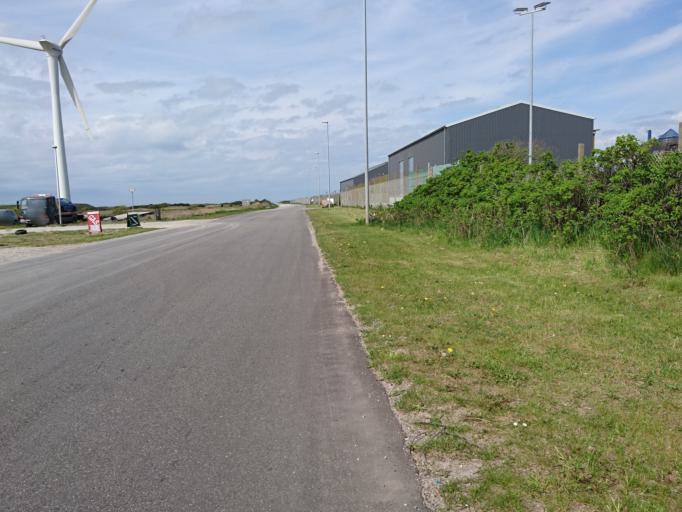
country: DK
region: North Denmark
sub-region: Frederikshavn Kommune
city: Skagen
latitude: 57.7360
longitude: 10.5675
